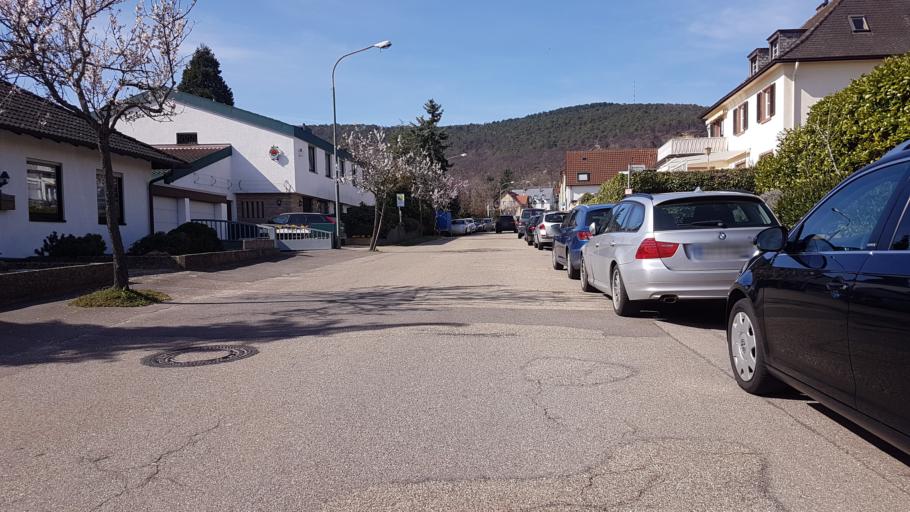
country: DE
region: Rheinland-Pfalz
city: Neustadt
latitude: 49.3671
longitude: 8.1514
